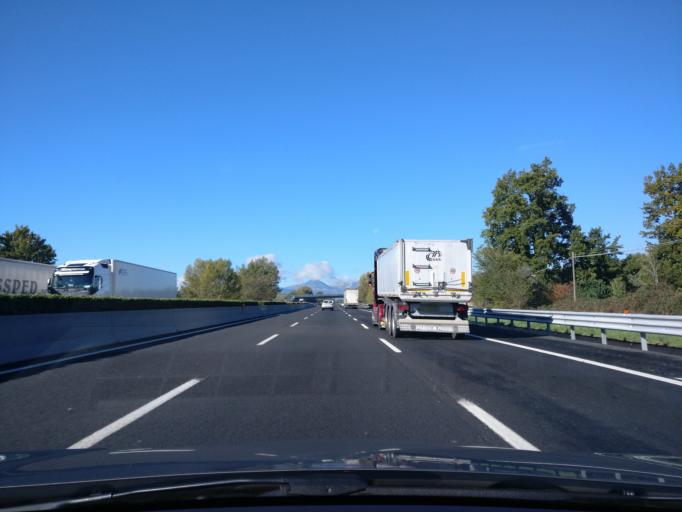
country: IT
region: Latium
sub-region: Provincia di Frosinone
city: Pofi
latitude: 41.5562
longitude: 13.4233
